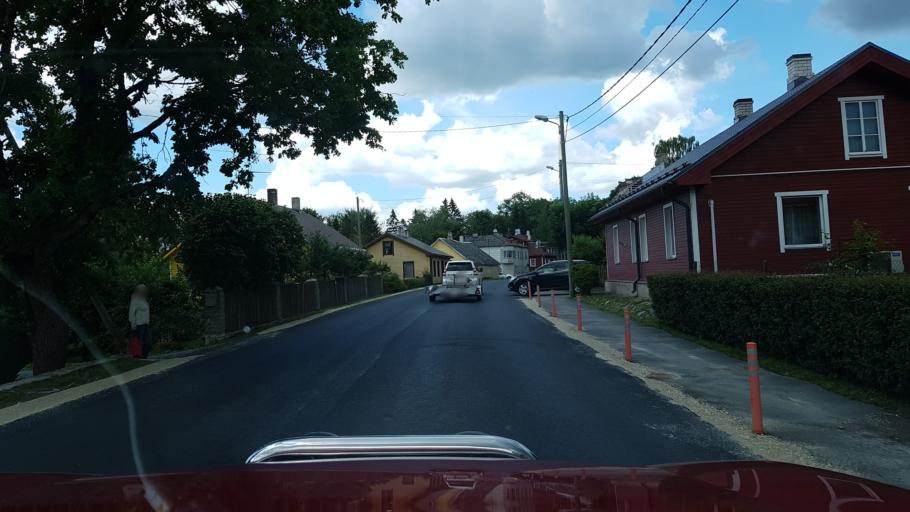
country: EE
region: Jaervamaa
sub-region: Jaerva-Jaani vald
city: Jarva-Jaani
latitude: 59.0355
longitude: 25.8780
